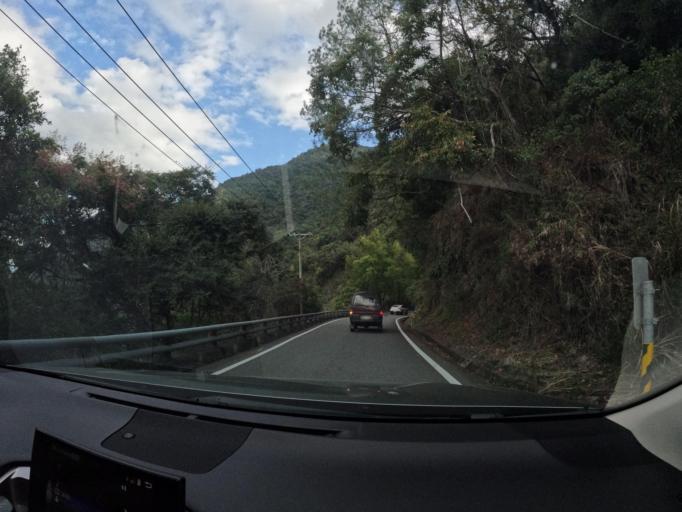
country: TW
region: Taiwan
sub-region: Taitung
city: Taitung
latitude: 23.1436
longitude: 121.0792
